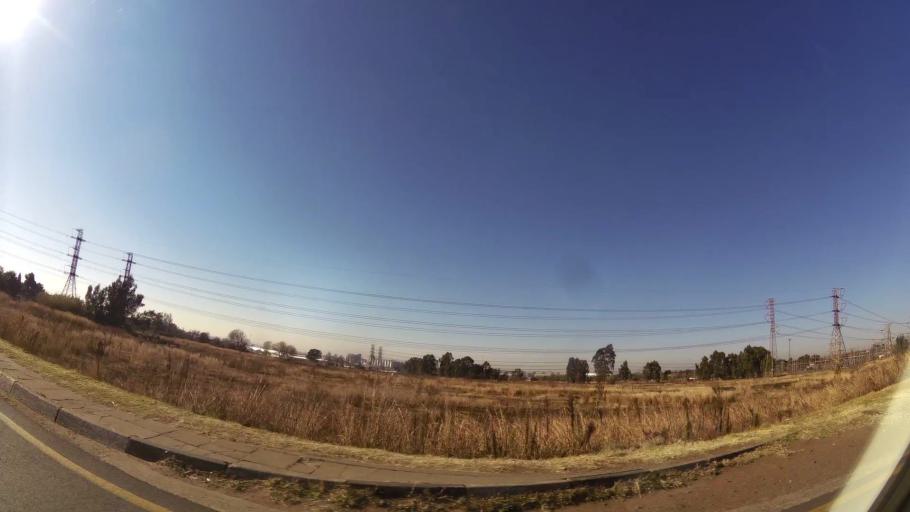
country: ZA
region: Gauteng
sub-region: Ekurhuleni Metropolitan Municipality
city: Germiston
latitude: -26.3036
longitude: 28.1159
